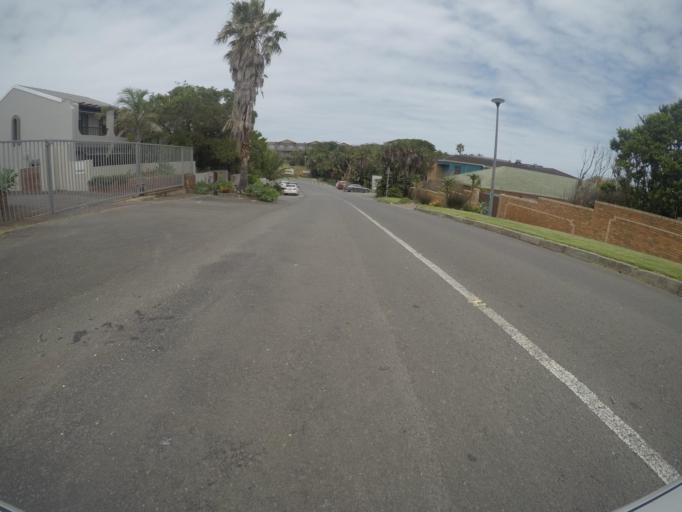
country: ZA
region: Eastern Cape
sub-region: Buffalo City Metropolitan Municipality
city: East London
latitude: -32.9822
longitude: 27.9510
